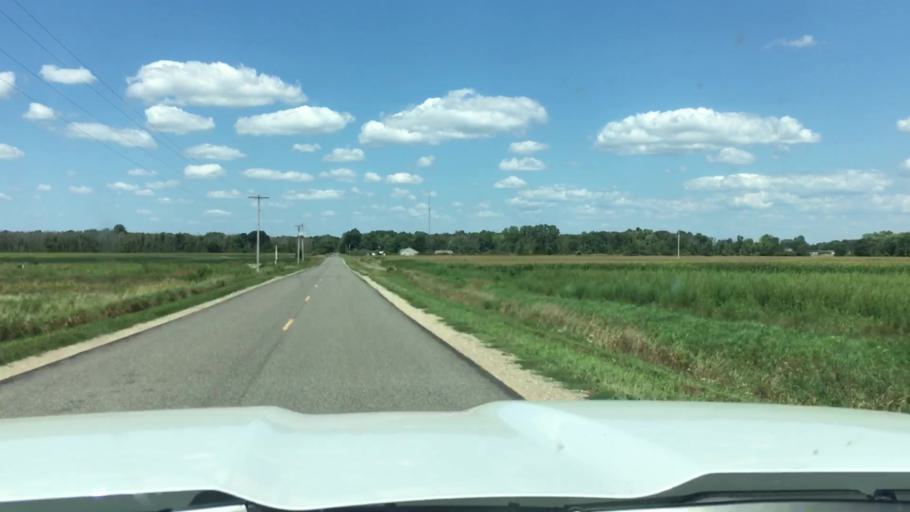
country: US
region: Michigan
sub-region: Muskegon County
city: Ravenna
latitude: 43.2666
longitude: -85.9180
